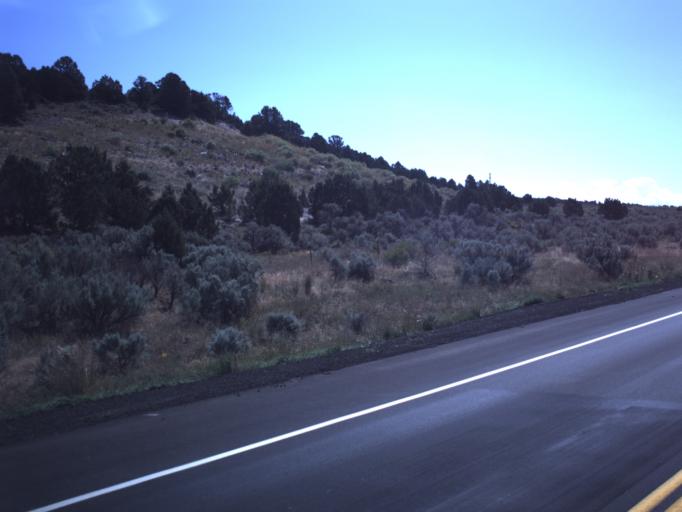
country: US
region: Utah
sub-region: Utah County
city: Genola
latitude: 39.9731
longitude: -112.2579
